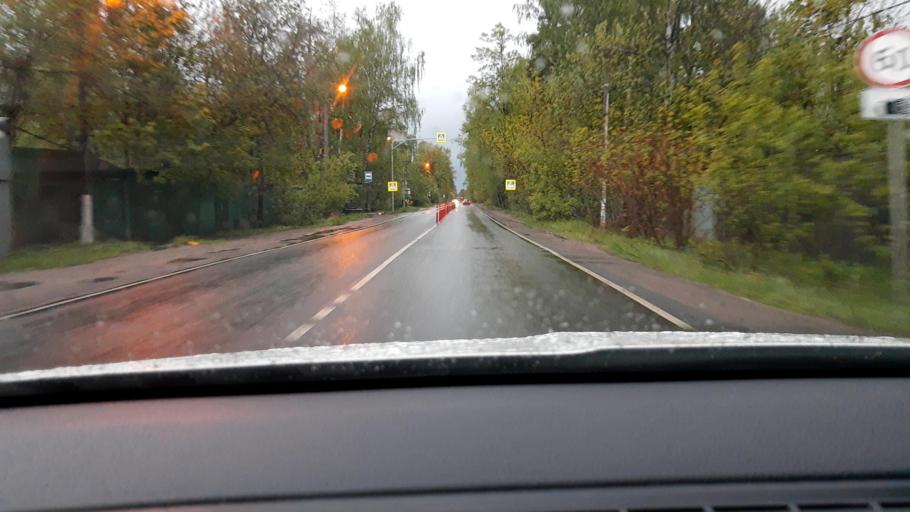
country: RU
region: Moskovskaya
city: Zagoryanskiy
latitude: 55.9189
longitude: 37.9154
